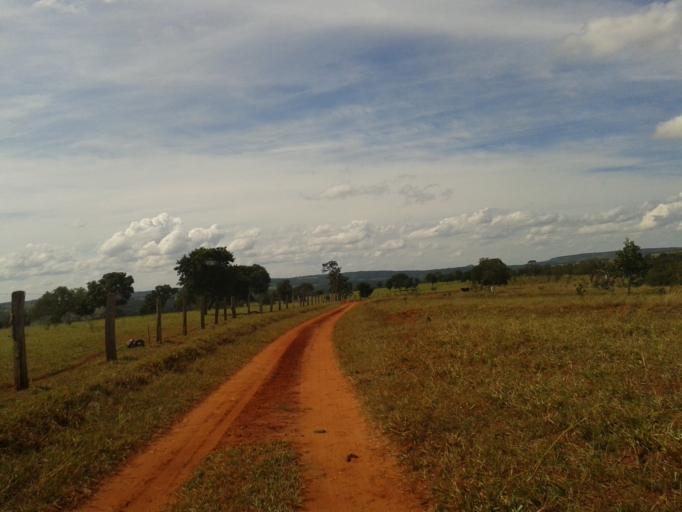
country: BR
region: Minas Gerais
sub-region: Campina Verde
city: Campina Verde
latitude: -19.4477
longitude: -49.6681
